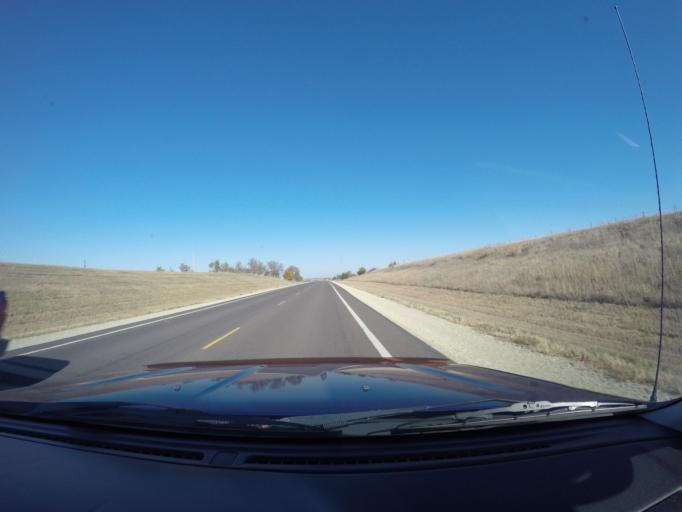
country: US
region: Kansas
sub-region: Marshall County
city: Blue Rapids
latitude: 39.6700
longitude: -96.7506
